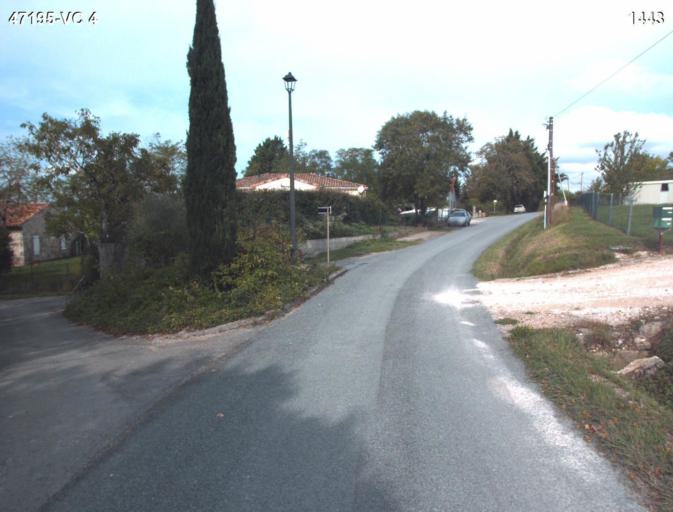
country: FR
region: Aquitaine
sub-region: Departement du Lot-et-Garonne
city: Nerac
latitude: 44.1091
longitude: 0.3832
